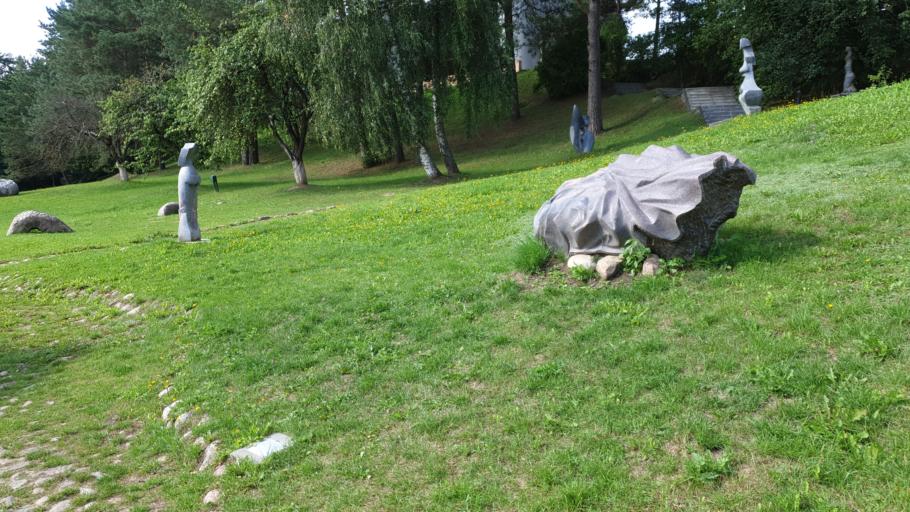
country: LT
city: Grigiskes
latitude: 54.7892
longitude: 25.0811
